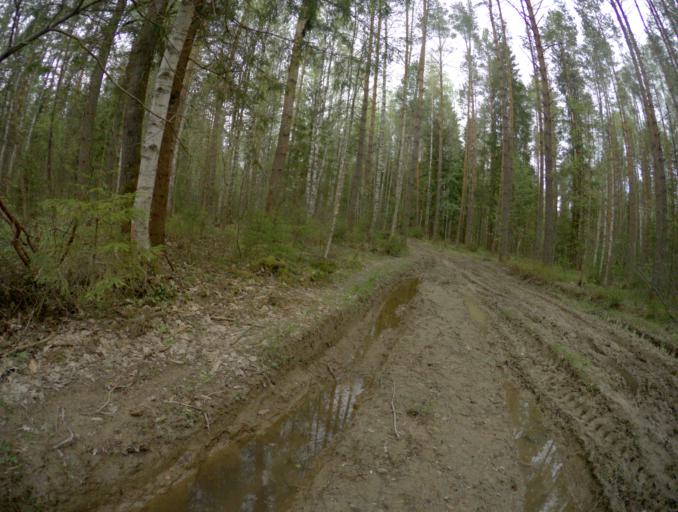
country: RU
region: Vladimir
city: Golovino
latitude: 55.9174
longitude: 40.5014
